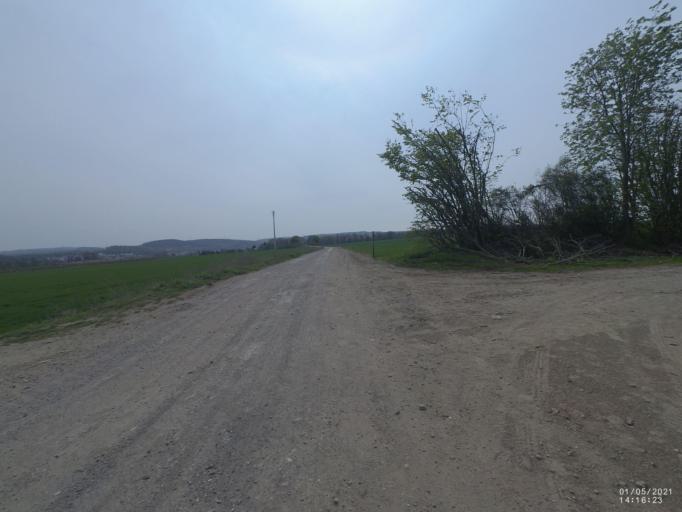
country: DE
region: Rheinland-Pfalz
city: Bassenheim
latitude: 50.3708
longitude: 7.4597
